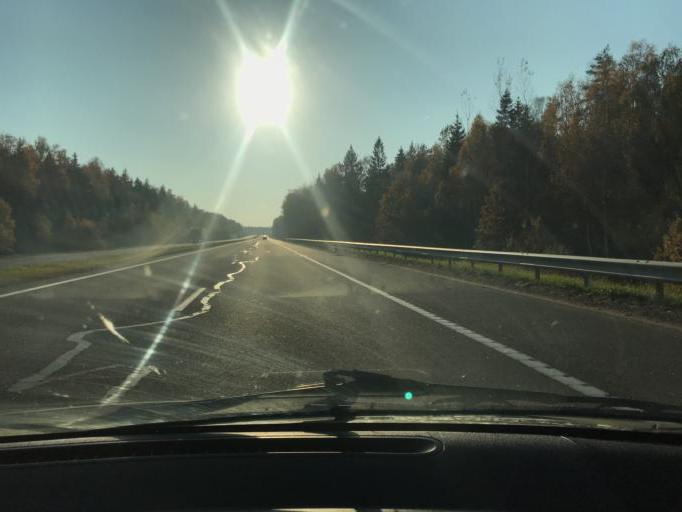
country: BY
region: Minsk
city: Loshnitsa
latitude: 54.2798
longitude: 28.7323
